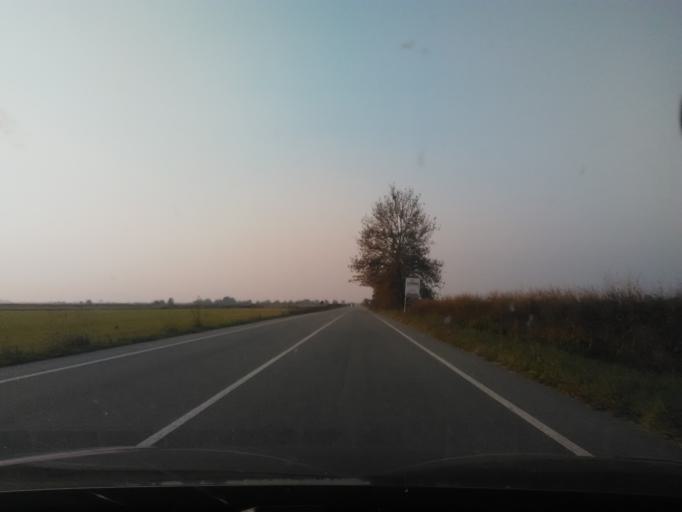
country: IT
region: Piedmont
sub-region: Provincia di Alessandria
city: Villanova Monferrato
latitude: 45.1931
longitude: 8.4697
